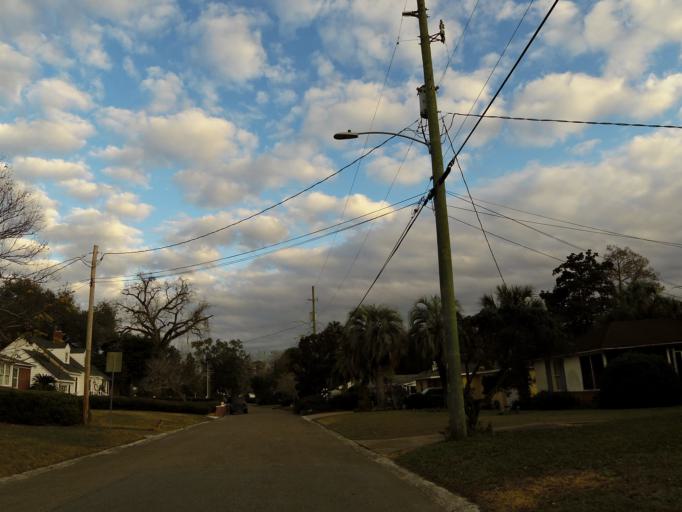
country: US
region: Florida
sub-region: Duval County
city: Jacksonville
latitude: 30.2912
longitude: -81.7175
